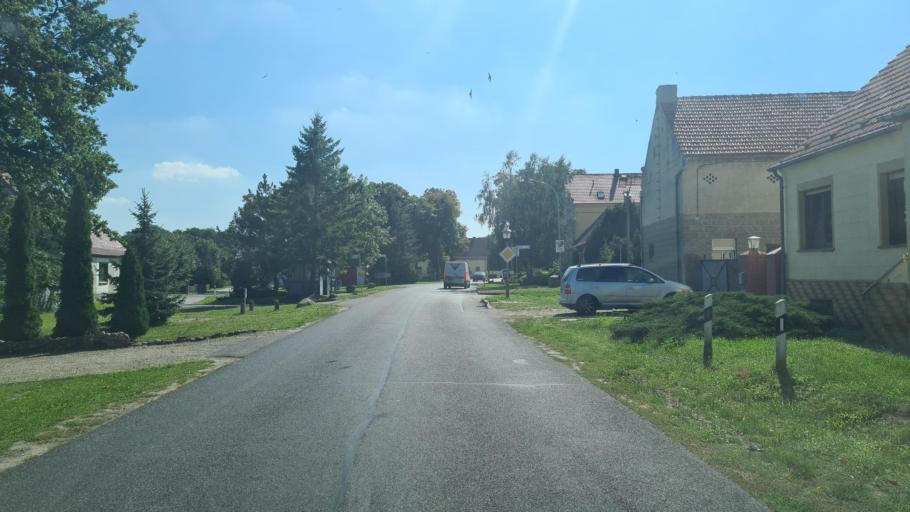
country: DE
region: Brandenburg
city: Friesack
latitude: 52.7121
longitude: 12.6431
